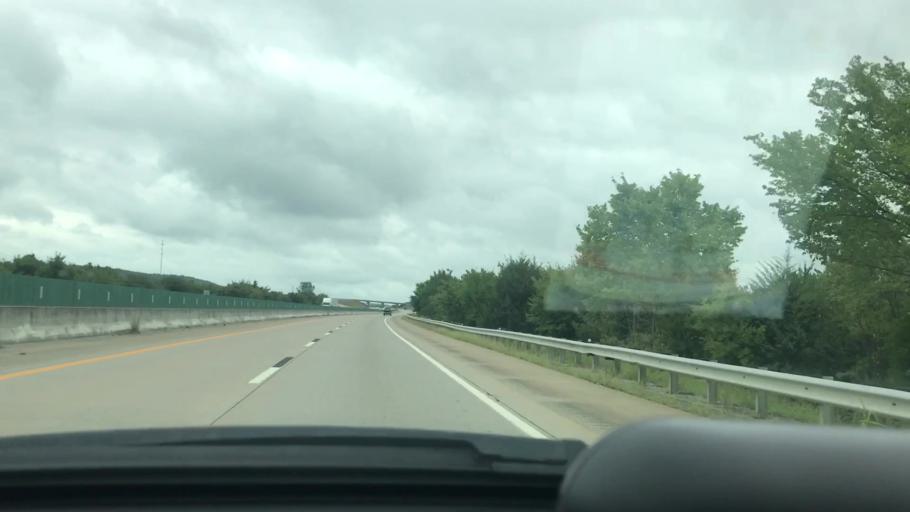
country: US
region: Oklahoma
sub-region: Pittsburg County
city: Krebs
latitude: 35.0502
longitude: -95.7092
